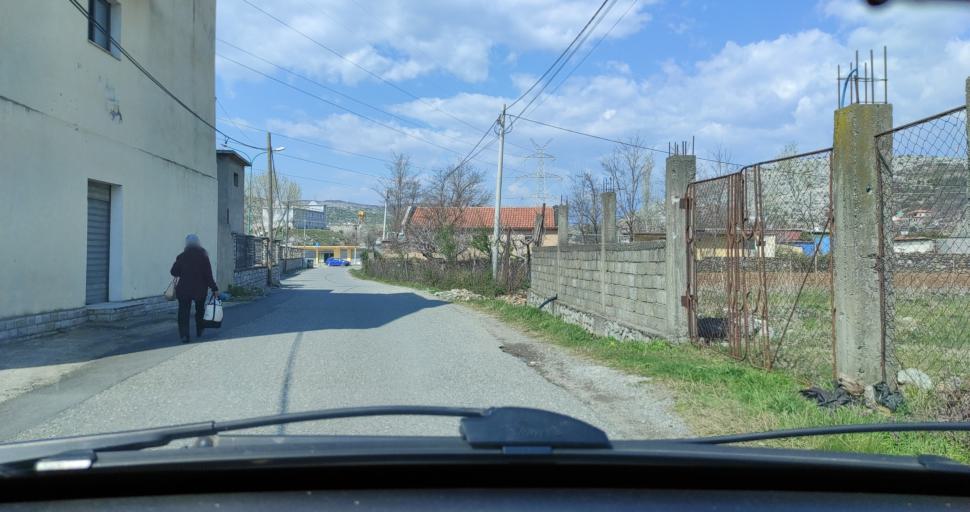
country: AL
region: Shkoder
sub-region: Rrethi i Shkodres
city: Vau i Dejes
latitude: 42.0068
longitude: 19.6418
